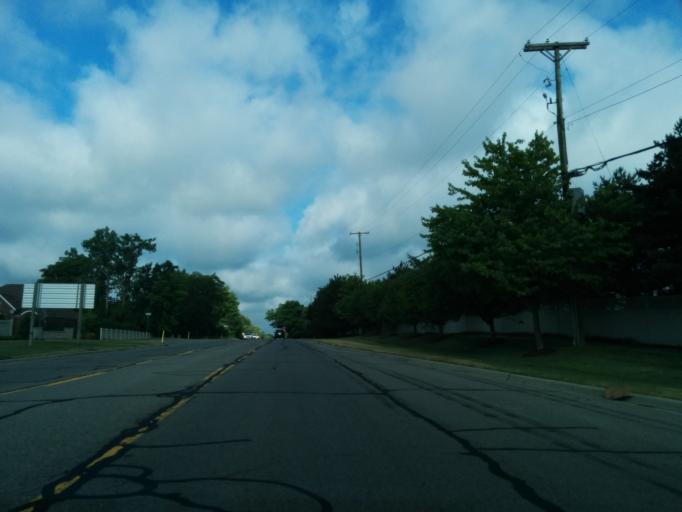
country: US
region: Michigan
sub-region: Oakland County
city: West Bloomfield Township
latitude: 42.5278
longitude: -83.3822
